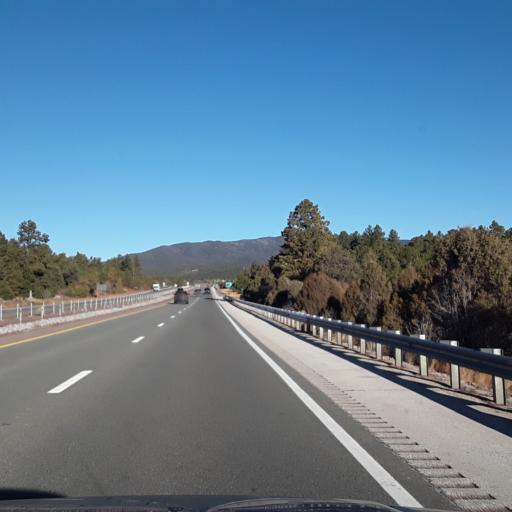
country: US
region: New Mexico
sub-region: San Miguel County
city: Pecos
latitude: 35.5720
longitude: -105.7595
